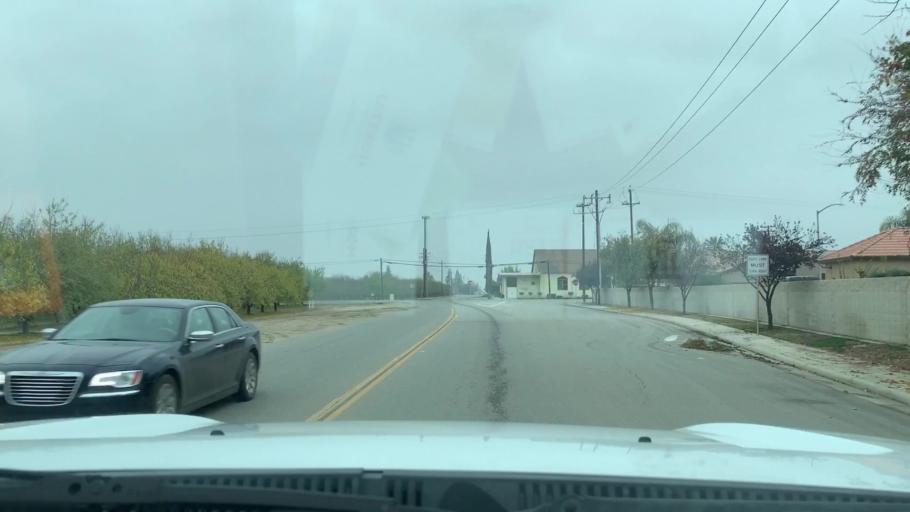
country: US
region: California
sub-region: Kern County
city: Shafter
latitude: 35.4988
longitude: -119.2961
